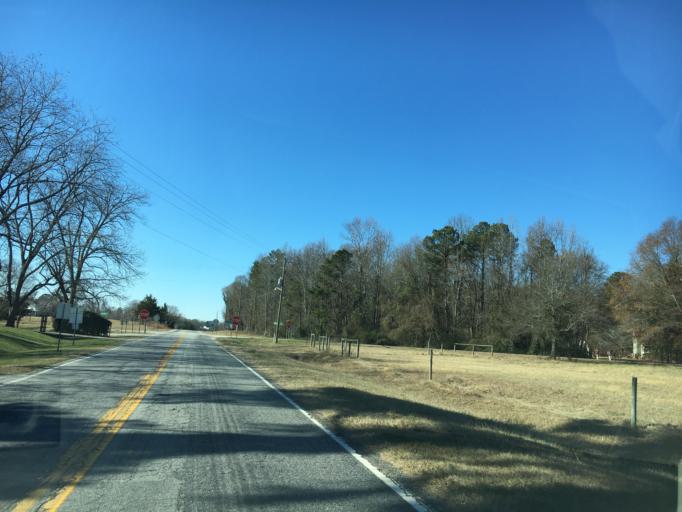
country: US
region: South Carolina
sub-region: Anderson County
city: Iva
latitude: 34.3783
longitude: -82.6993
